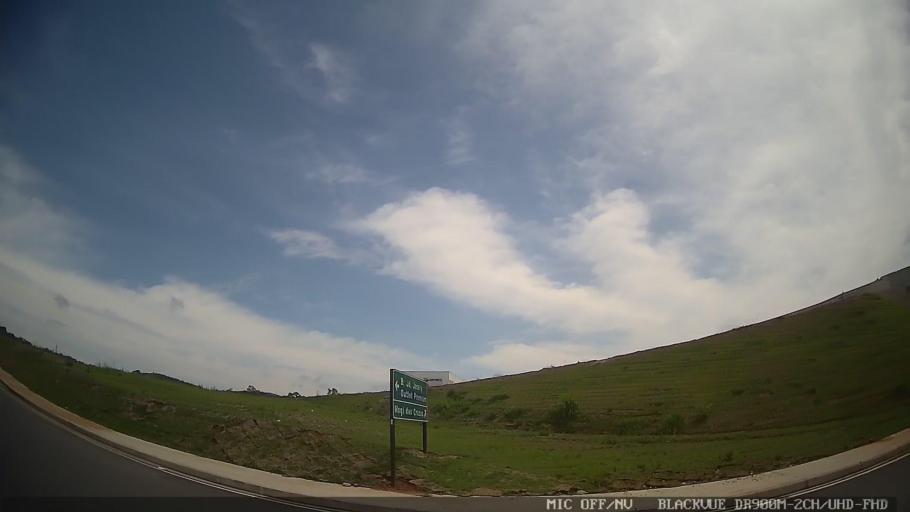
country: BR
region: Sao Paulo
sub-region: Aruja
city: Aruja
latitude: -23.4340
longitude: -46.2687
